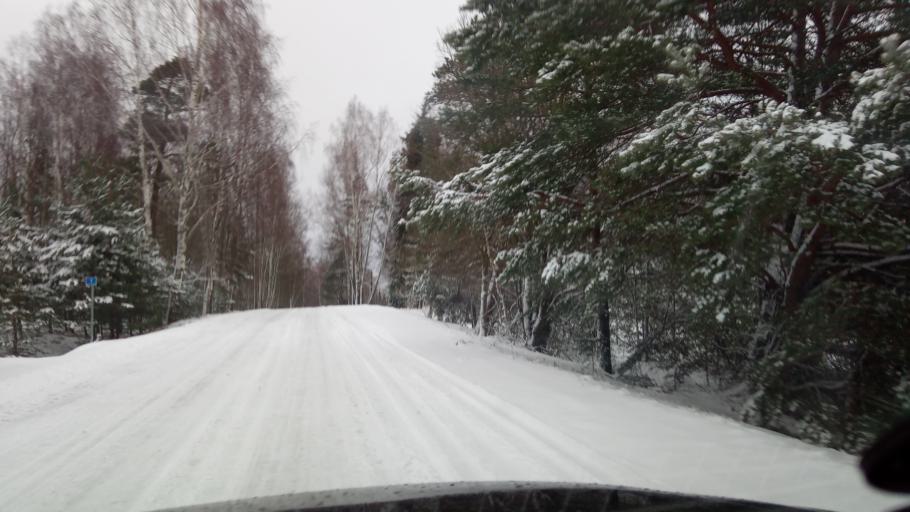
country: LT
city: Zarasai
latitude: 55.6217
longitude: 25.9539
